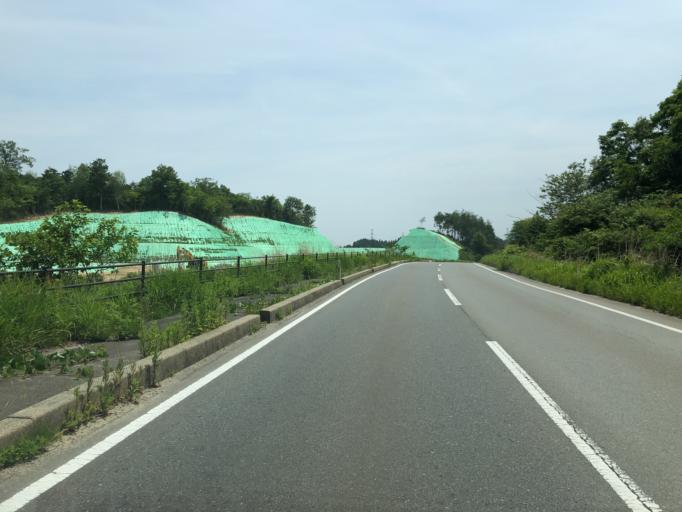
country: JP
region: Fukushima
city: Namie
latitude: 37.5451
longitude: 140.9365
